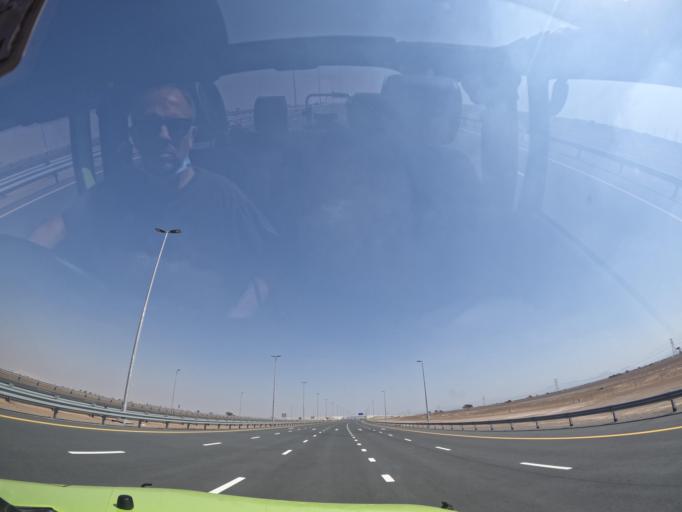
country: AE
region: Ash Shariqah
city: Adh Dhayd
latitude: 24.9253
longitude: 55.8089
